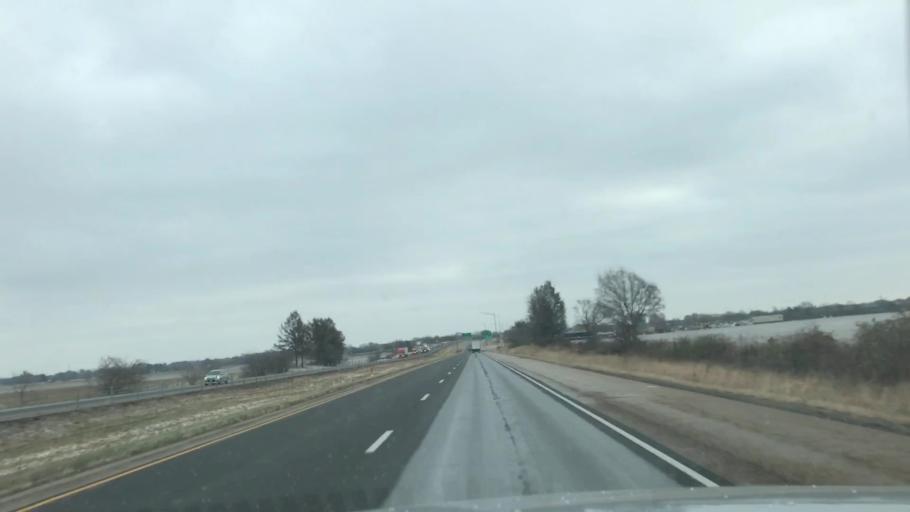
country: US
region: Illinois
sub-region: Madison County
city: Troy
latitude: 38.7517
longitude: -89.9181
